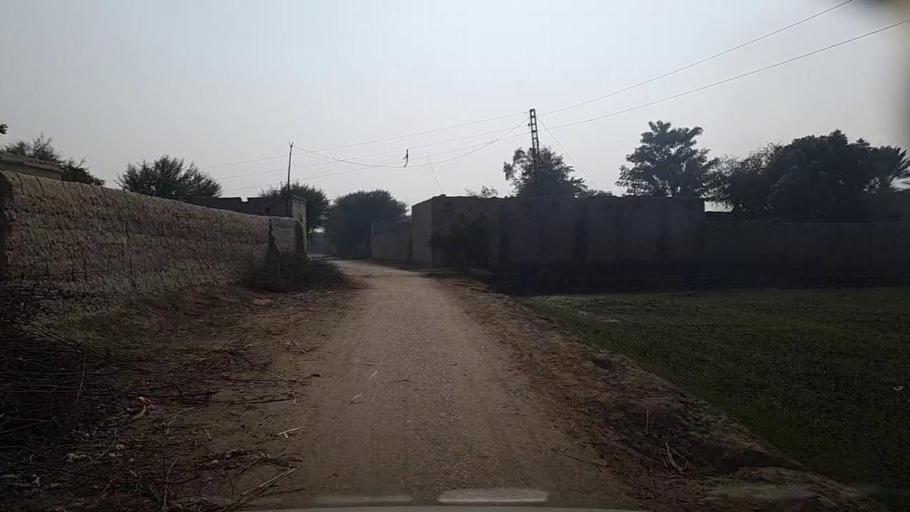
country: PK
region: Sindh
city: Setharja Old
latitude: 27.1252
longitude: 68.5155
